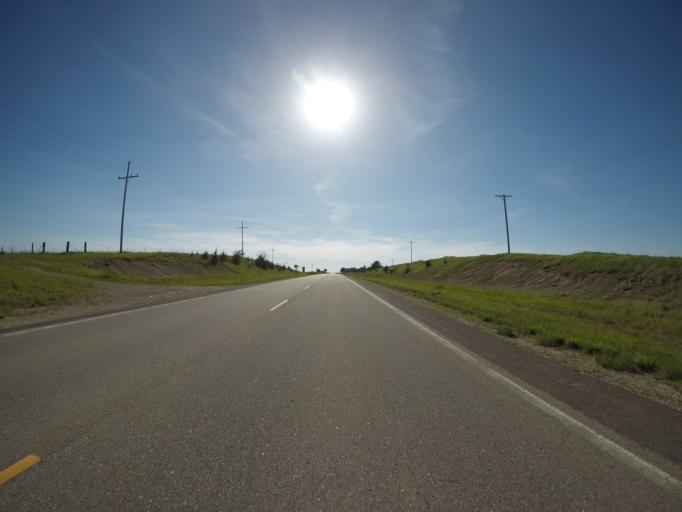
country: US
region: Kansas
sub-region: Clay County
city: Clay Center
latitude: 39.3647
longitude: -96.9190
